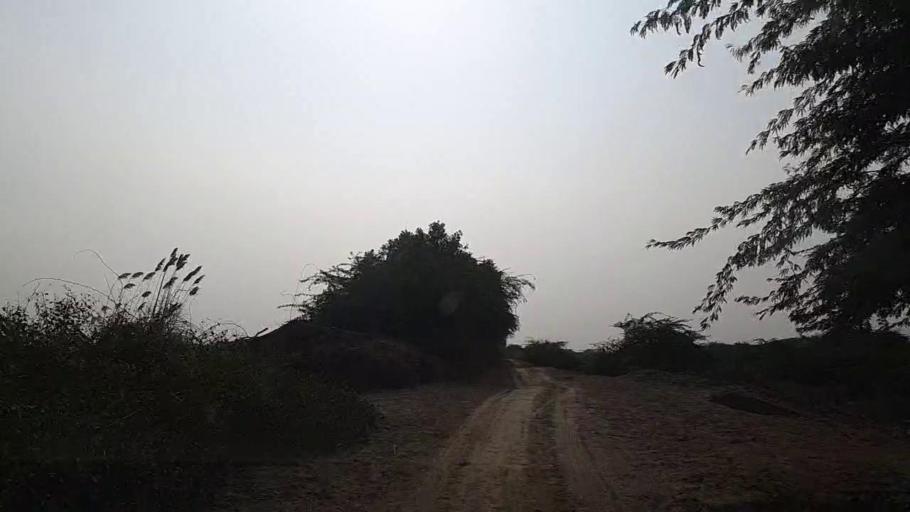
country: PK
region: Sindh
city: Gharo
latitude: 24.6576
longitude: 67.6226
